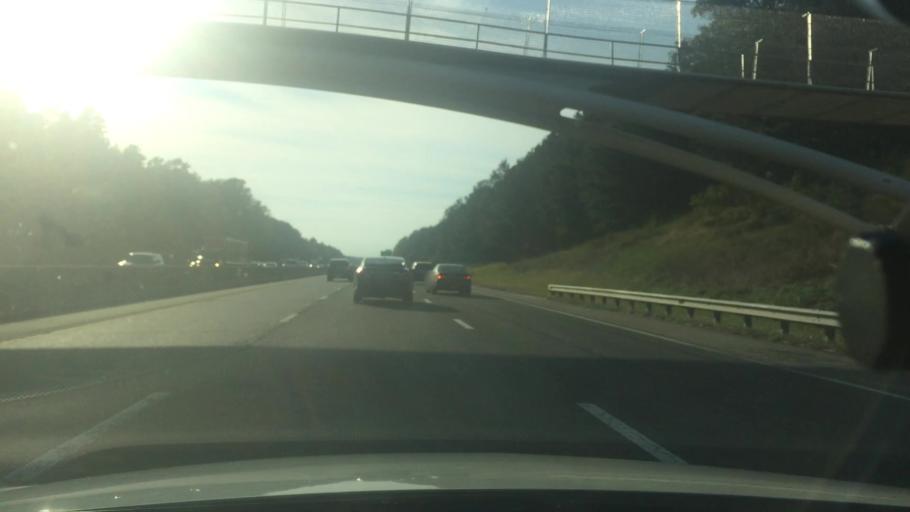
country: US
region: North Carolina
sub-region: Durham County
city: Durham
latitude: 35.9075
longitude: -78.9430
